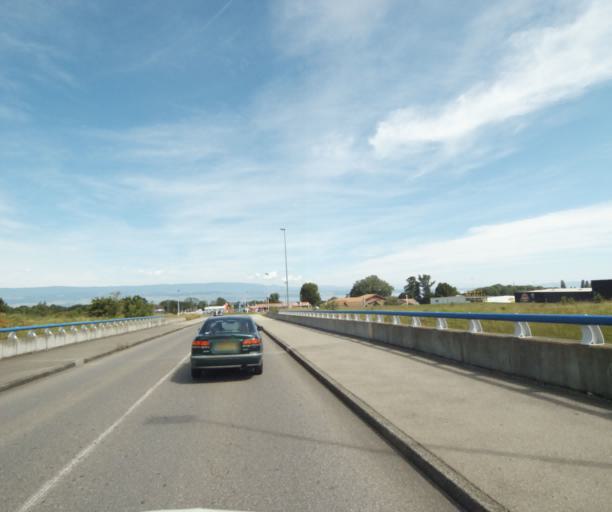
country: FR
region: Rhone-Alpes
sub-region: Departement de la Haute-Savoie
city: Margencel
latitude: 46.3468
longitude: 6.4331
